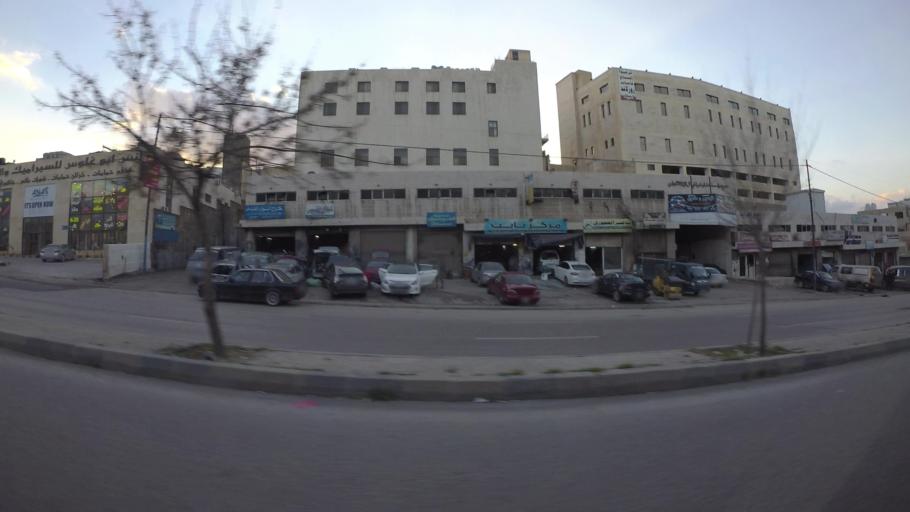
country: JO
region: Amman
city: Al Bunayyat ash Shamaliyah
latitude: 31.9214
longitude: 35.9118
